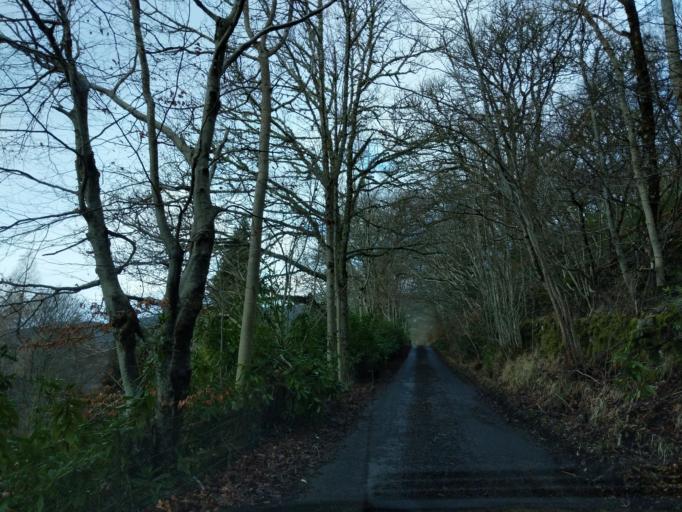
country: GB
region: Scotland
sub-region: Perth and Kinross
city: Comrie
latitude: 56.5742
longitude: -4.0707
